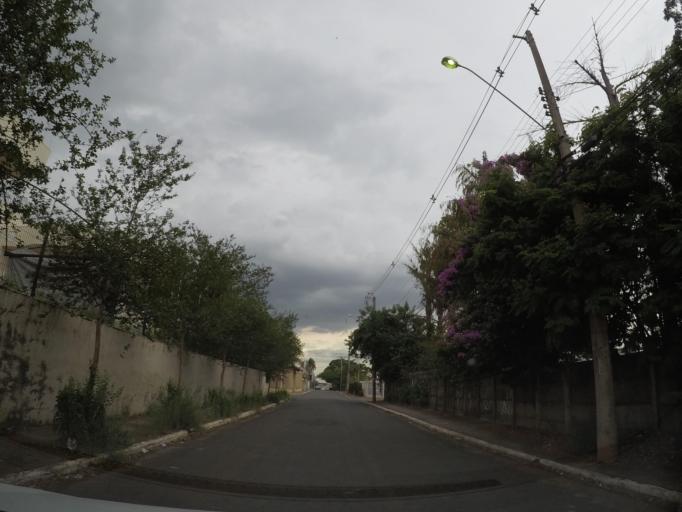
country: BR
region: Sao Paulo
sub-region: Sumare
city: Sumare
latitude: -22.8146
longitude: -47.2462
